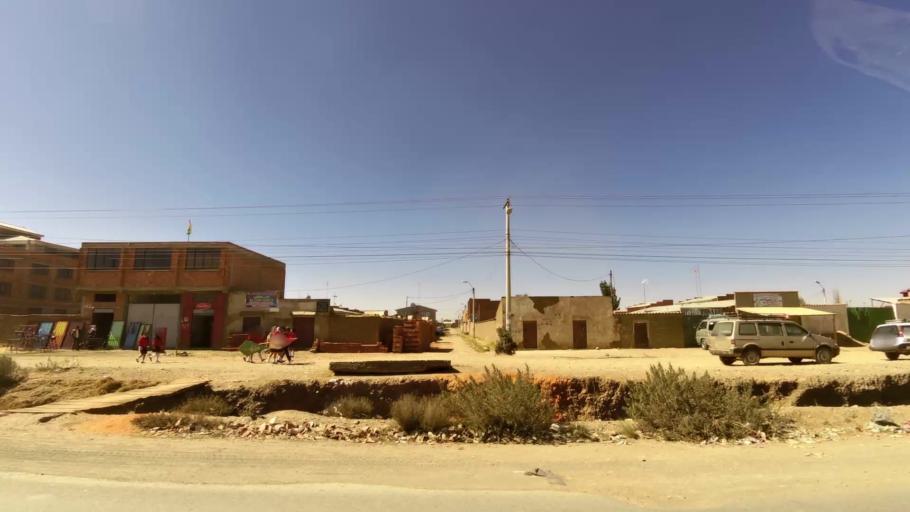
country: BO
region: La Paz
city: La Paz
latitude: -16.5743
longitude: -68.2272
